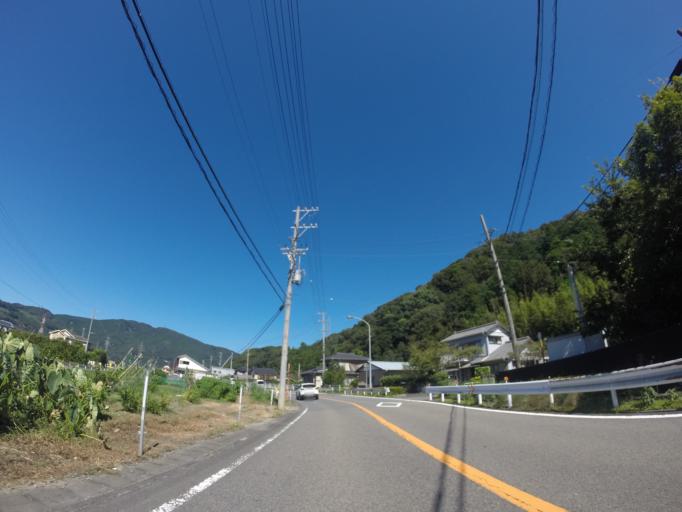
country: JP
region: Shizuoka
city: Kanaya
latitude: 34.8680
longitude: 138.1221
